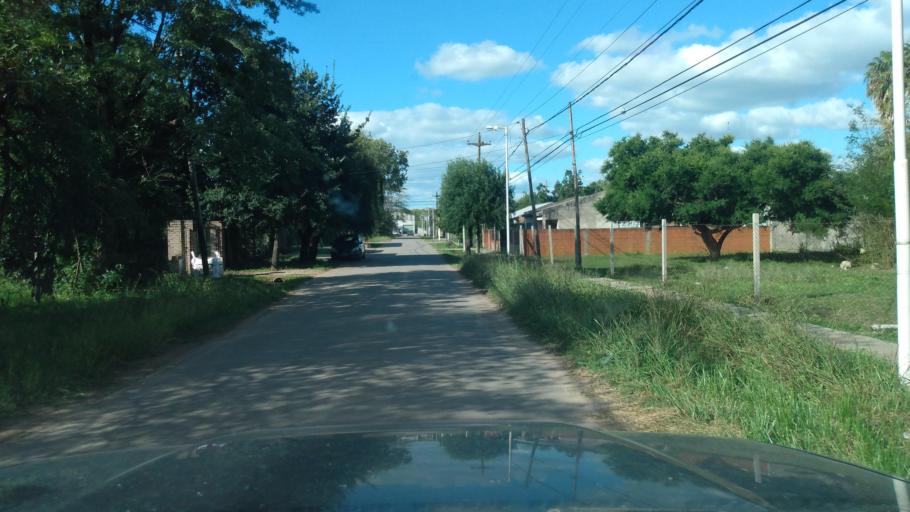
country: AR
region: Buenos Aires
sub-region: Partido de Lujan
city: Lujan
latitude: -34.5825
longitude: -59.0938
